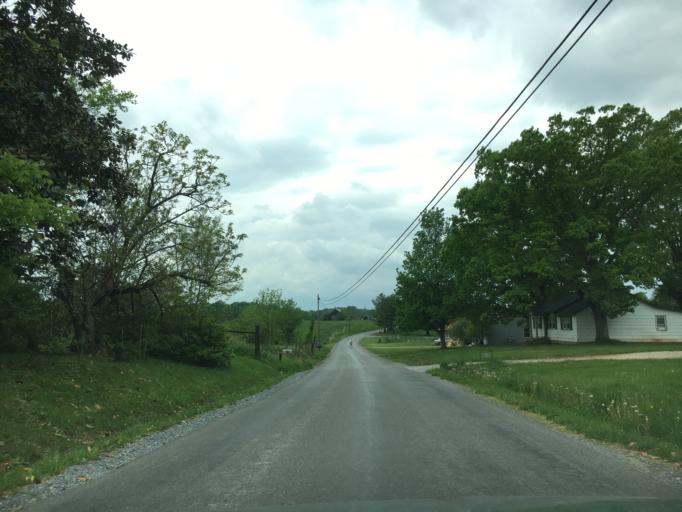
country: US
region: Virginia
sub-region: Campbell County
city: Rustburg
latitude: 37.1668
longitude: -79.0525
